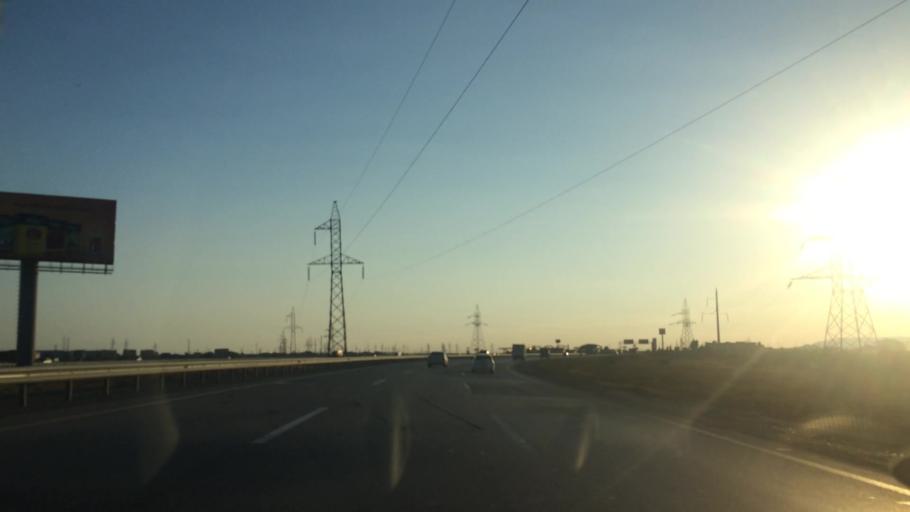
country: AZ
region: Baki
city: Qobustan
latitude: 39.9696
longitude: 49.4136
